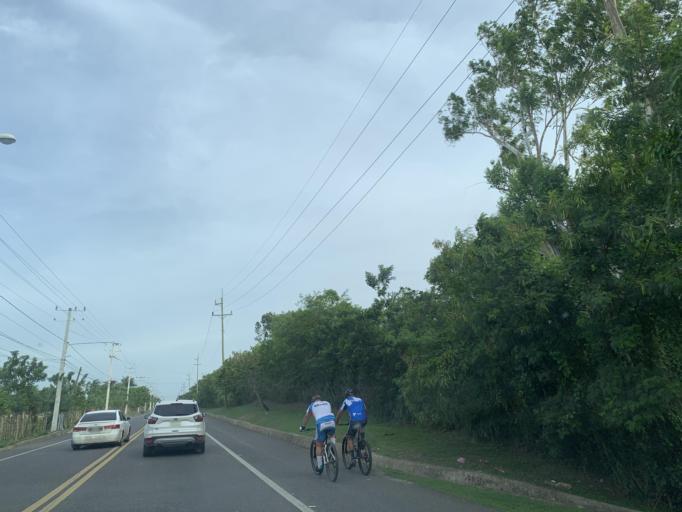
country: DO
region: Puerto Plata
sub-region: Puerto Plata
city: Puerto Plata
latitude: 19.7330
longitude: -70.6280
